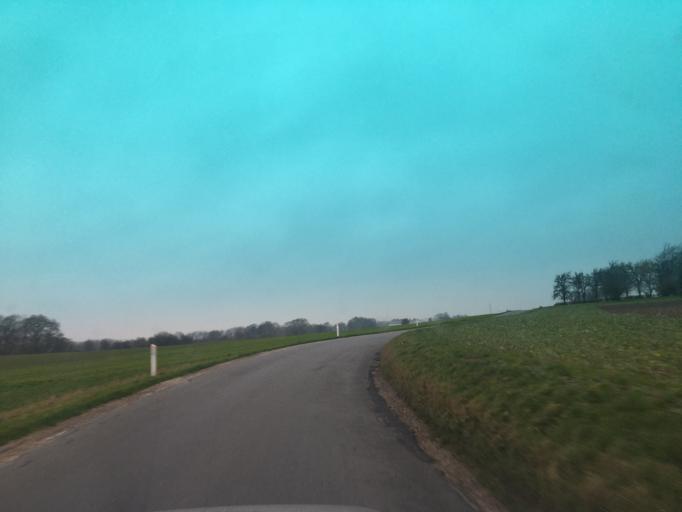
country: DK
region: Zealand
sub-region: Naestved Kommune
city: Fuglebjerg
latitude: 55.2825
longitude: 11.4360
